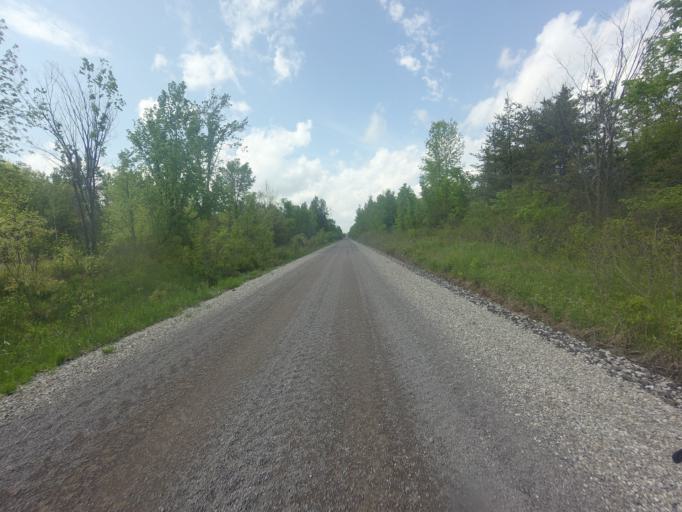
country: CA
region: Ontario
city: Carleton Place
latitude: 45.0601
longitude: -76.0937
